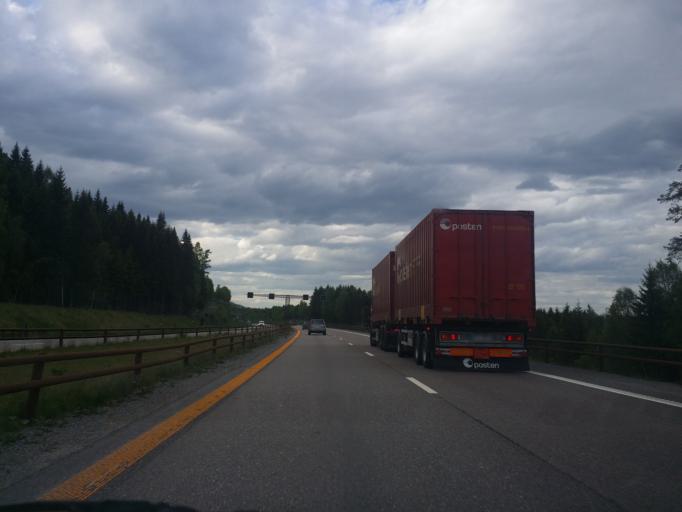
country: NO
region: Akershus
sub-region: Eidsvoll
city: Eidsvoll
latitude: 60.3483
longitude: 11.2086
